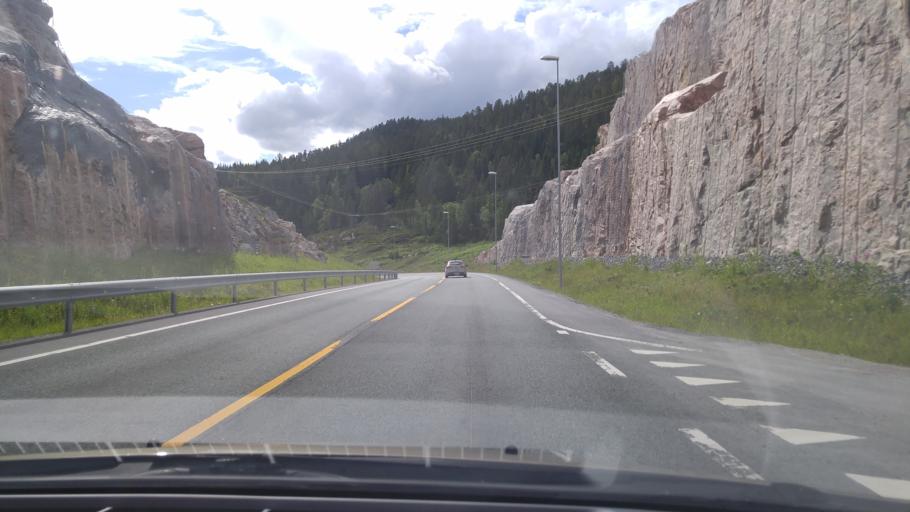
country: NO
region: Nord-Trondelag
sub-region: Namsos
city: Namsos
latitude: 64.3803
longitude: 11.3814
